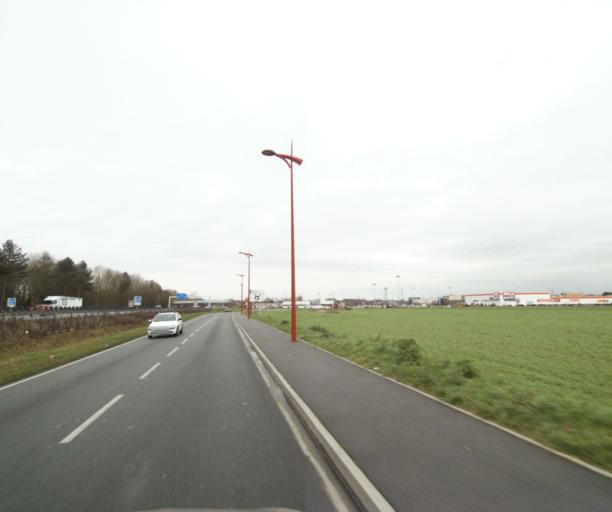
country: FR
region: Nord-Pas-de-Calais
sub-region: Departement du Nord
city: Petite-Foret
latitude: 50.3721
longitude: 3.4792
